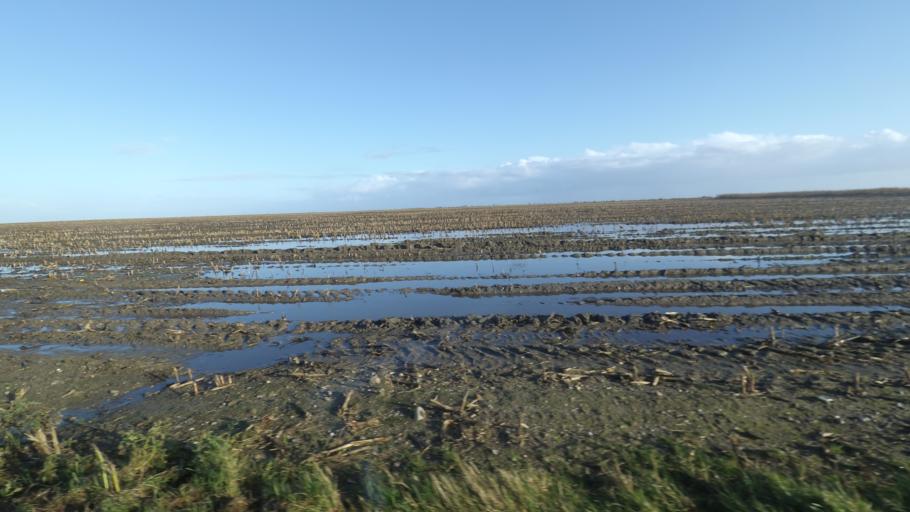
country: DK
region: Central Jutland
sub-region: Odder Kommune
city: Odder
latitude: 55.8442
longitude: 10.1923
